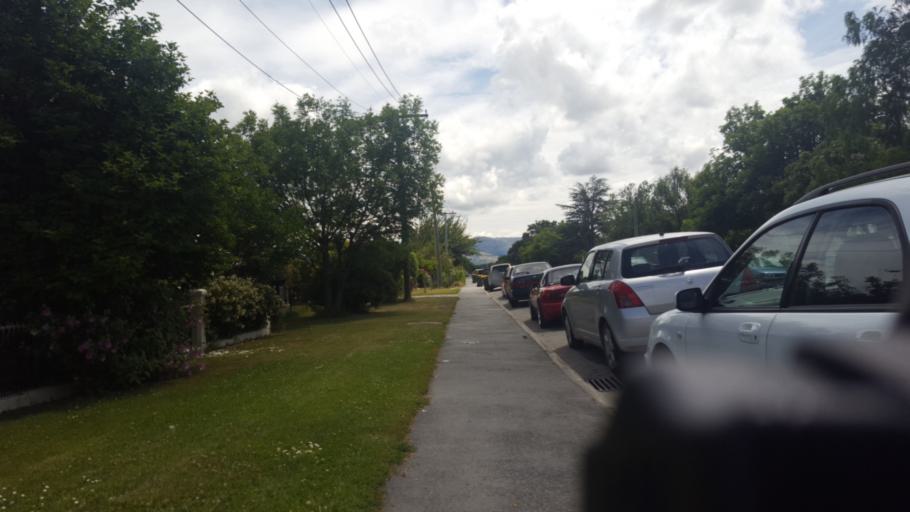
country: NZ
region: Otago
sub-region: Queenstown-Lakes District
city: Wanaka
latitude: -45.2565
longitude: 169.3896
